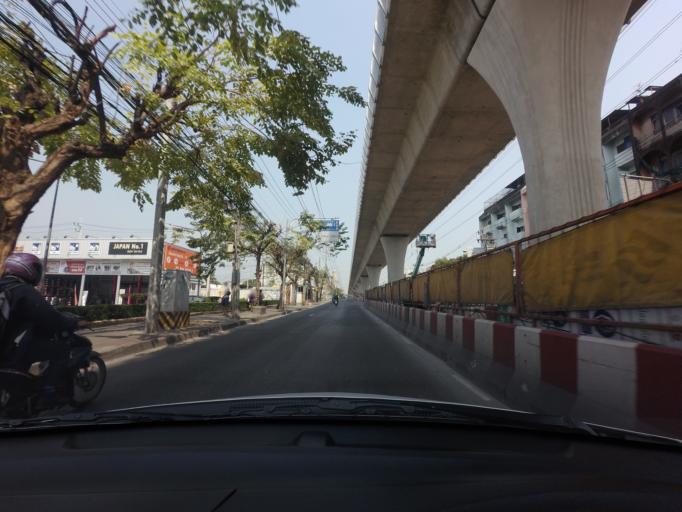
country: TH
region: Bangkok
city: Bangkok Yai
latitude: 13.7422
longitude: 100.4705
